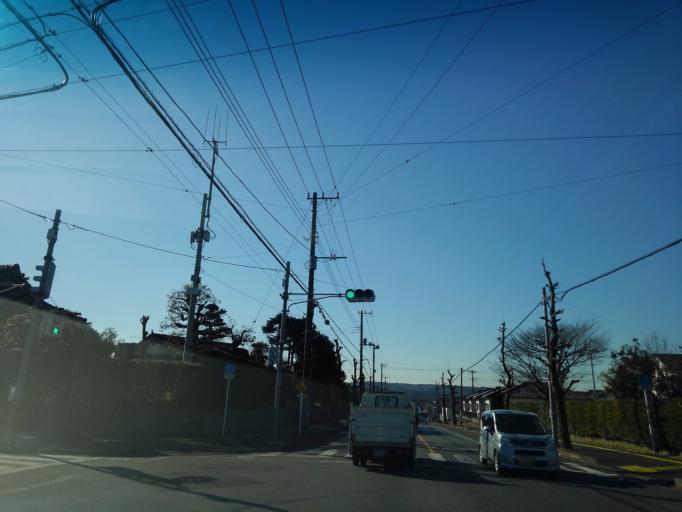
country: JP
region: Chiba
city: Kimitsu
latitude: 35.3292
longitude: 139.9148
